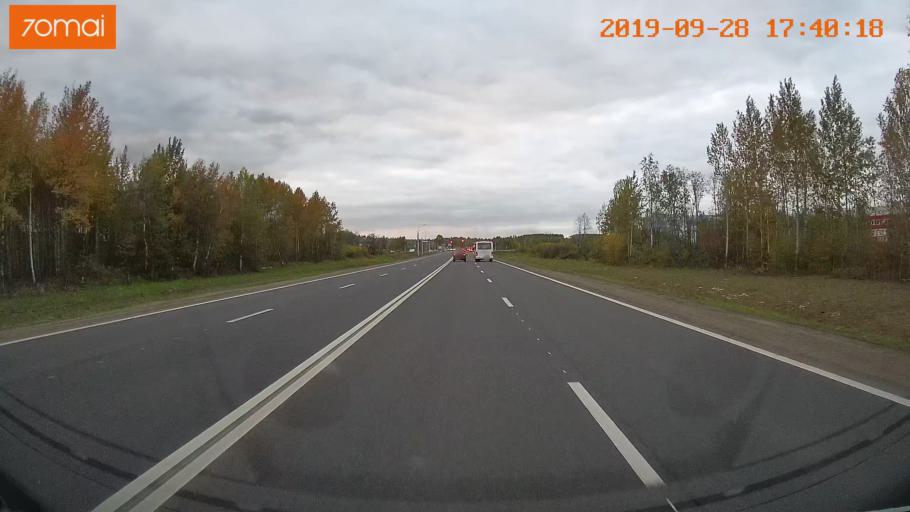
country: RU
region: Jaroslavl
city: Yaroslavl
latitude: 57.5493
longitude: 39.8975
